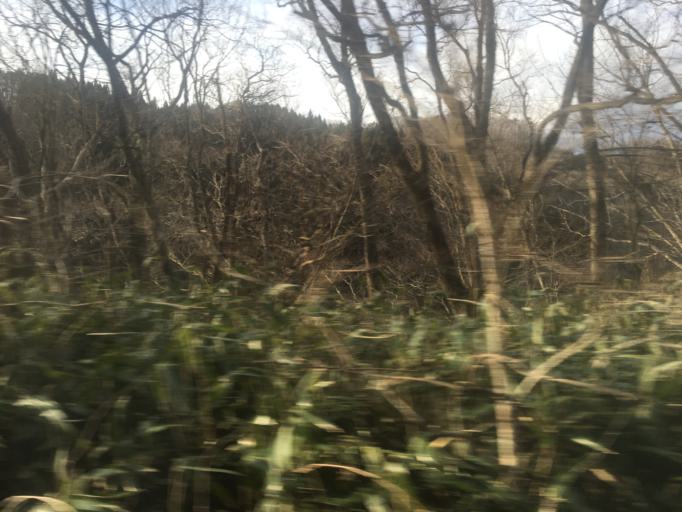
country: JP
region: Fukushima
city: Funehikimachi-funehiki
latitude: 37.2312
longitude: 140.6916
